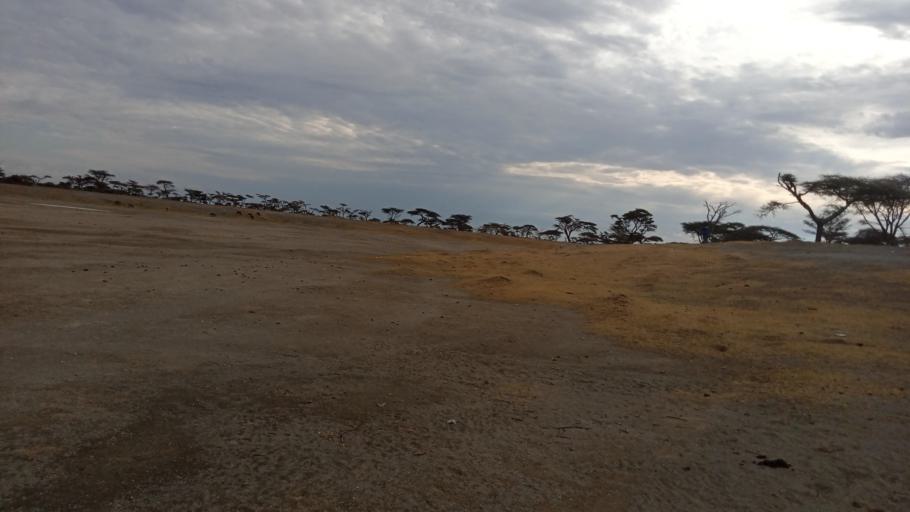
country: ET
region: Oromiya
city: Ziway
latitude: 7.6891
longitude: 38.6542
